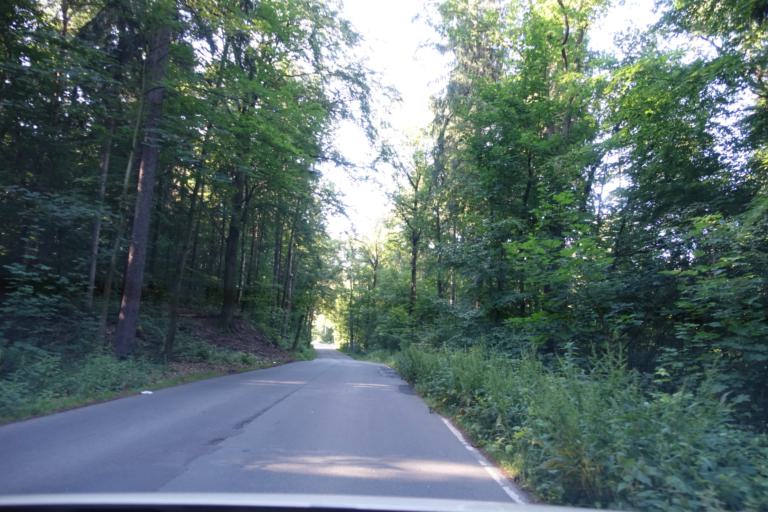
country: DE
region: Saxony
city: Hilbersdorf
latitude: 50.8478
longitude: 12.9617
